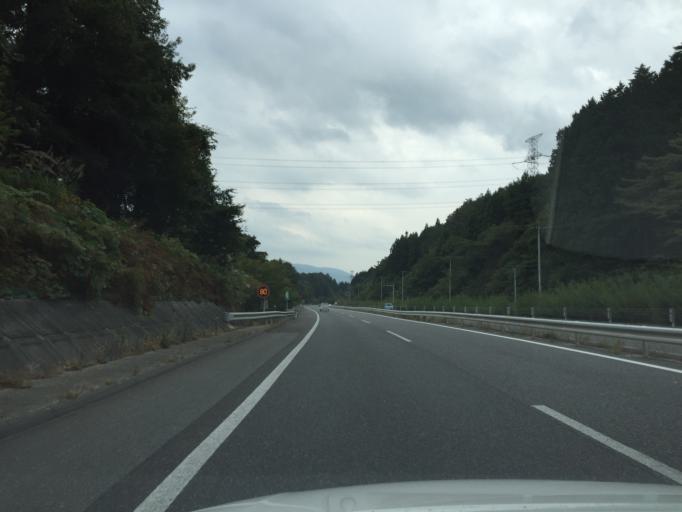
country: JP
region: Fukushima
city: Iwaki
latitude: 37.1658
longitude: 140.7269
